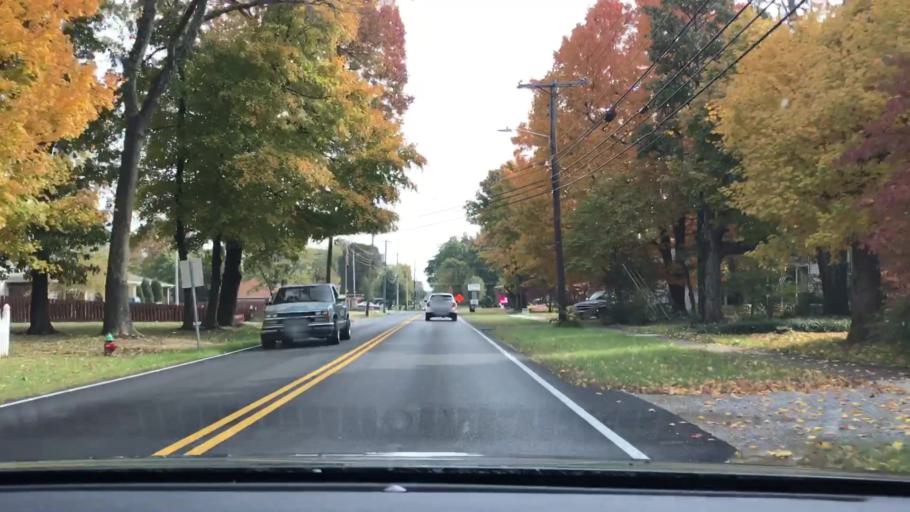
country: US
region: Kentucky
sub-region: Graves County
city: Mayfield
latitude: 36.7418
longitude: -88.6550
